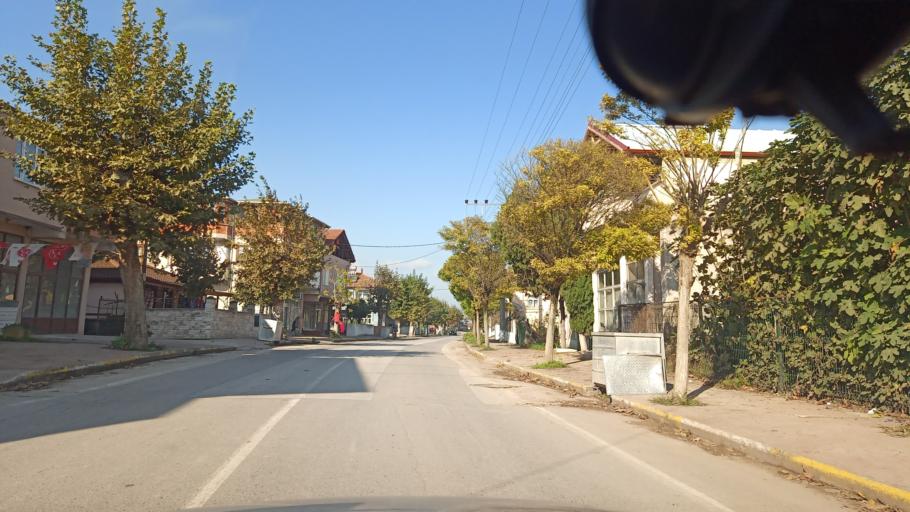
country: TR
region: Sakarya
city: Sogutlu
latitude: 40.9065
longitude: 30.4739
